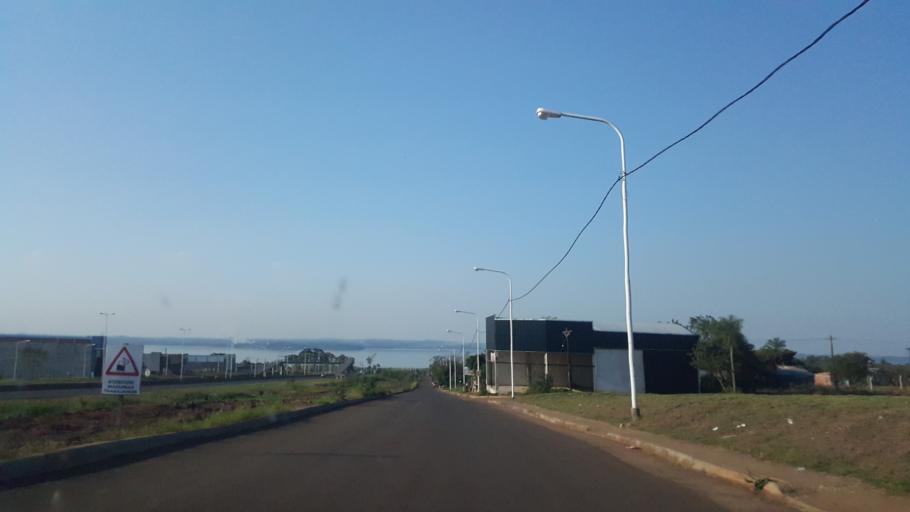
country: AR
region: Misiones
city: Garupa
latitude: -27.4512
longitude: -55.8554
